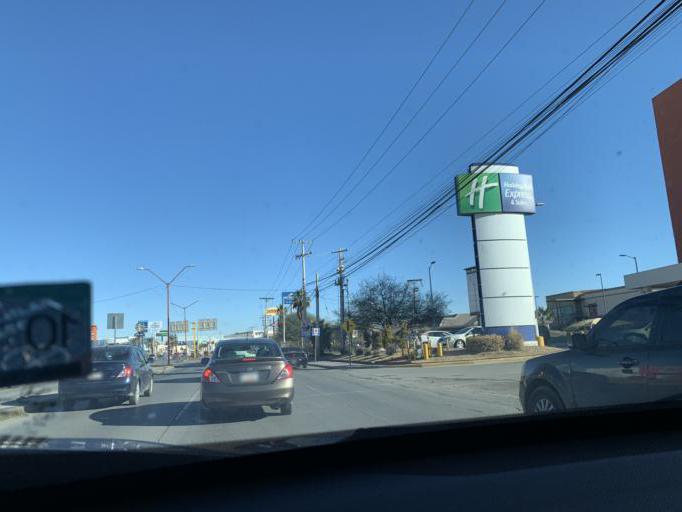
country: MX
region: Chihuahua
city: Ciudad Juarez
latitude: 31.6849
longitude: -106.4069
